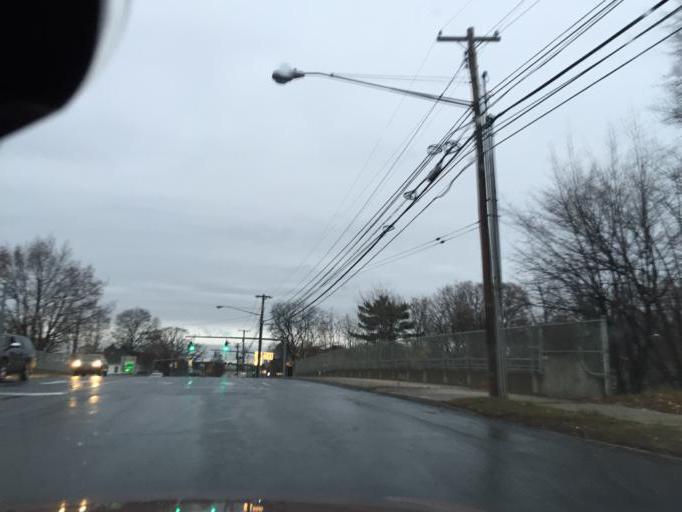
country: US
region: Connecticut
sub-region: Fairfield County
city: East Norwalk
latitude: 41.1082
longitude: -73.4060
